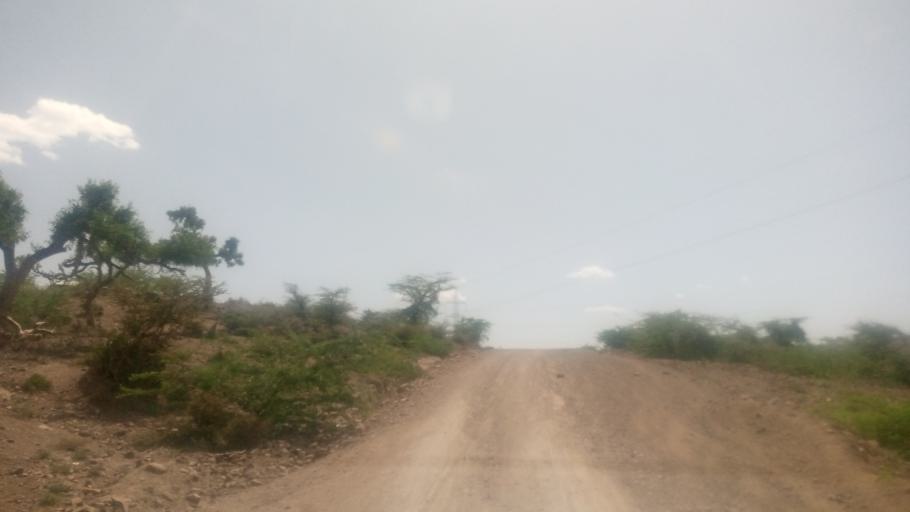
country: ET
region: Oromiya
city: Deder
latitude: 9.5275
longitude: 41.3560
